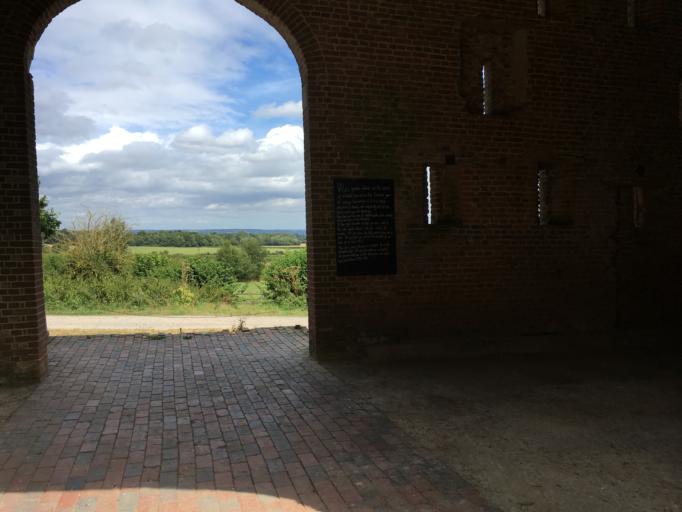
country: GB
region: England
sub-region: Kent
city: Cranbrook
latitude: 51.1163
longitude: 0.5815
